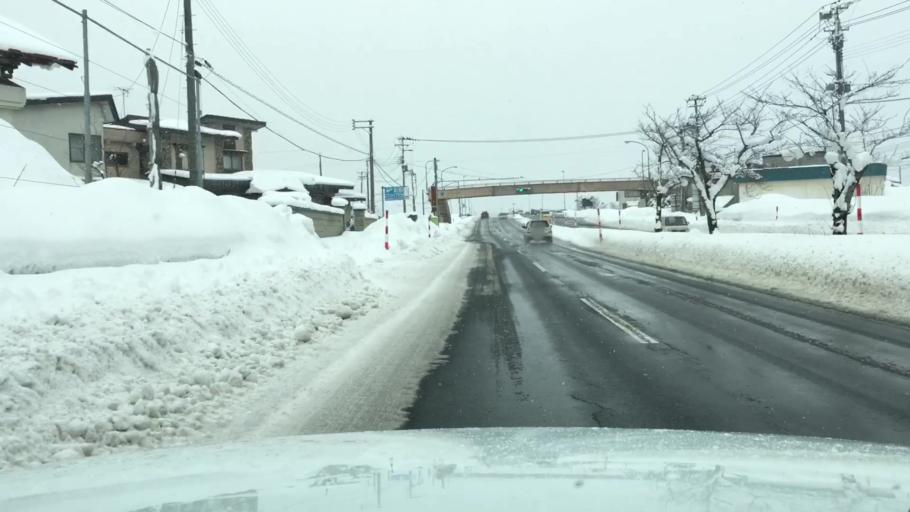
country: JP
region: Aomori
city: Hirosaki
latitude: 40.6431
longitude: 140.4927
